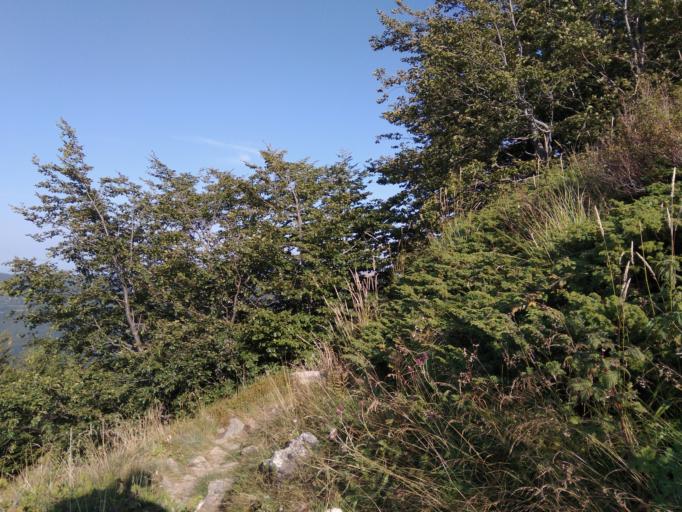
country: BG
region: Stara Zagora
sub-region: Obshtina Pavel Banya
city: Asen
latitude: 42.7626
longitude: 25.1073
